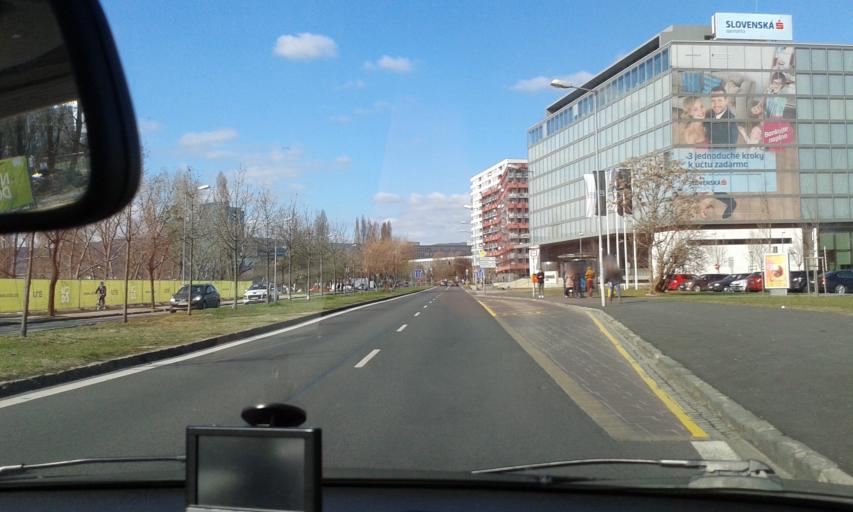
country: SK
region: Bratislavsky
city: Bratislava
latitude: 48.1660
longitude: 17.1503
